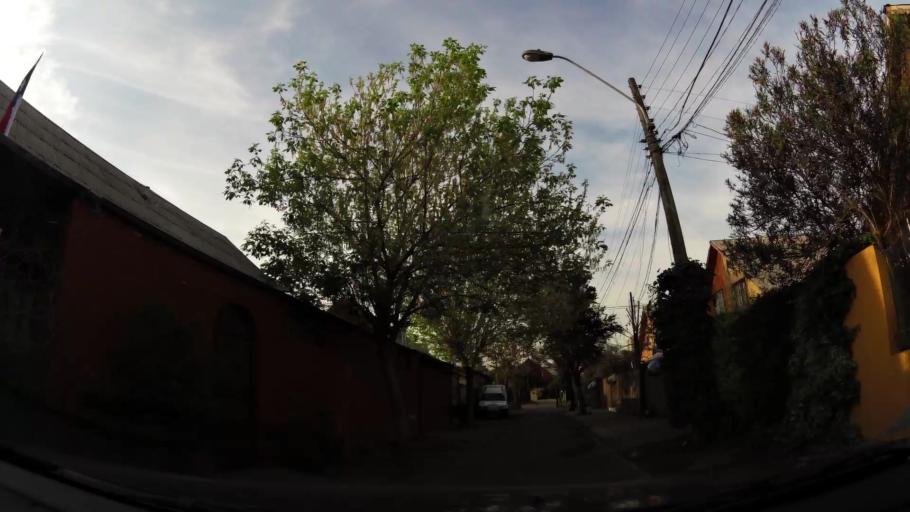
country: CL
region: Santiago Metropolitan
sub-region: Provincia de Santiago
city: Villa Presidente Frei, Nunoa, Santiago, Chile
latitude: -33.5193
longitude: -70.5883
